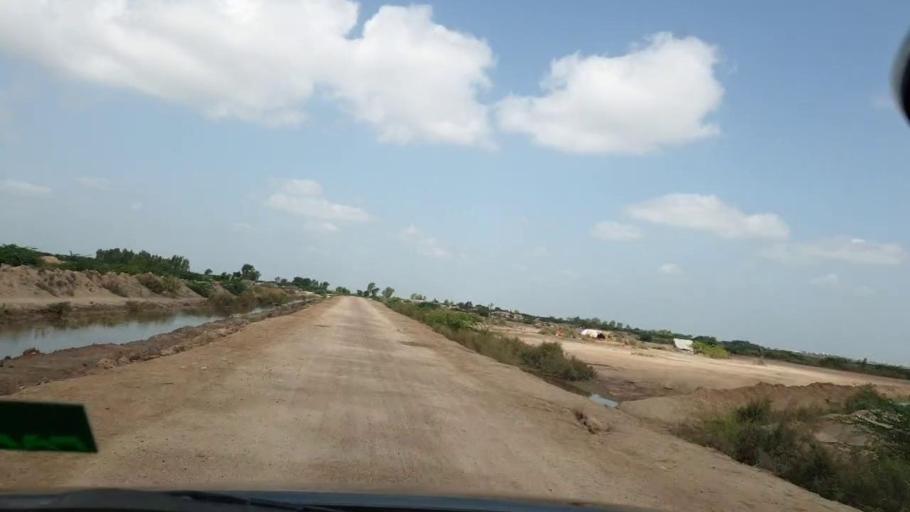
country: PK
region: Sindh
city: Kadhan
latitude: 24.6023
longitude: 69.1218
